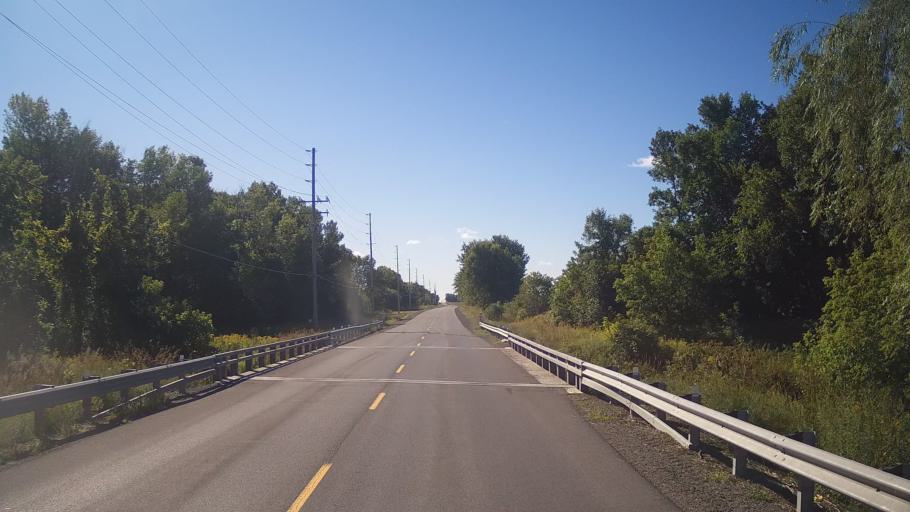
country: CA
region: Ontario
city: Prescott
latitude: 44.9803
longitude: -75.5407
